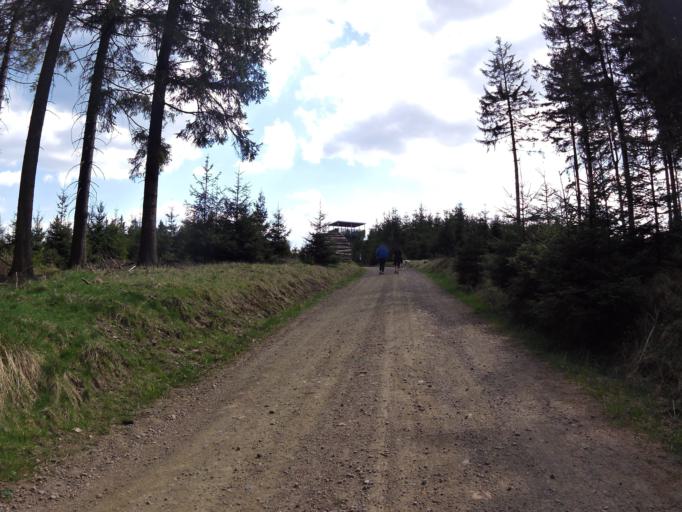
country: DE
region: Thuringia
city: Unterschonau
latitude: 50.7662
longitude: 10.5629
